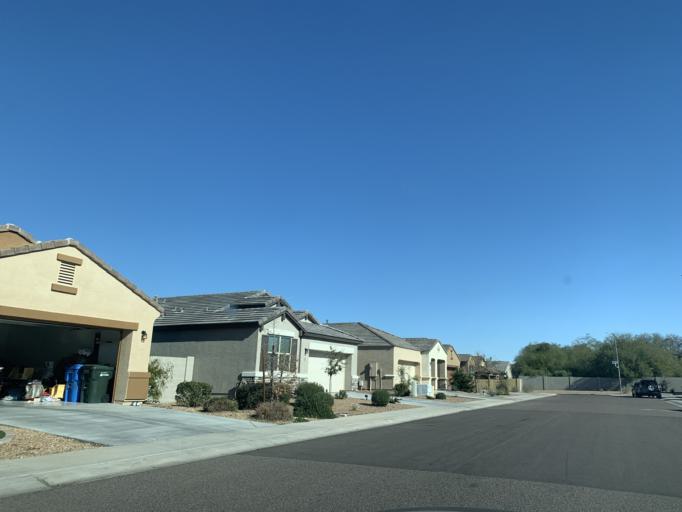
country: US
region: Arizona
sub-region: Maricopa County
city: Laveen
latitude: 33.3928
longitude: -112.1224
